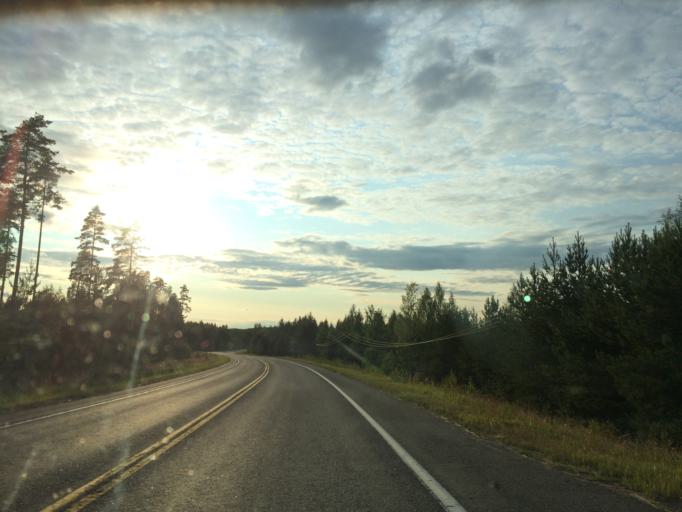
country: FI
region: Haeme
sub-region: Haemeenlinna
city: Janakkala
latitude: 60.8572
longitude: 24.5975
